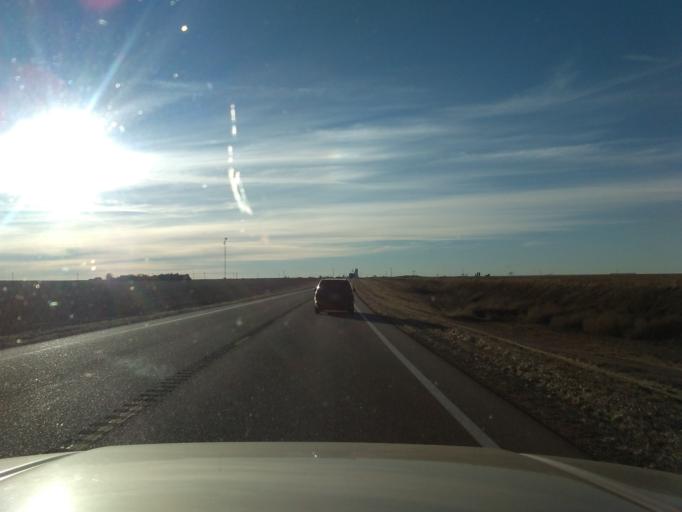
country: US
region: Kansas
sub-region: Thomas County
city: Colby
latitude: 39.4570
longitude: -100.7861
